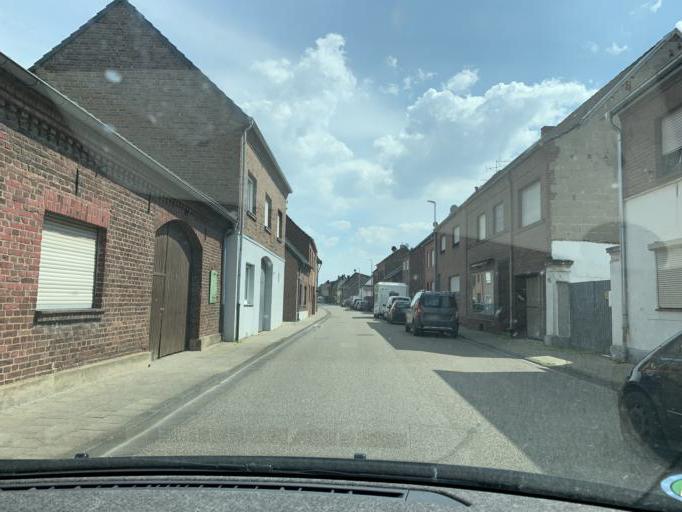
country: DE
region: North Rhine-Westphalia
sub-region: Regierungsbezirk Koln
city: Elsdorf
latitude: 50.9241
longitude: 6.5868
